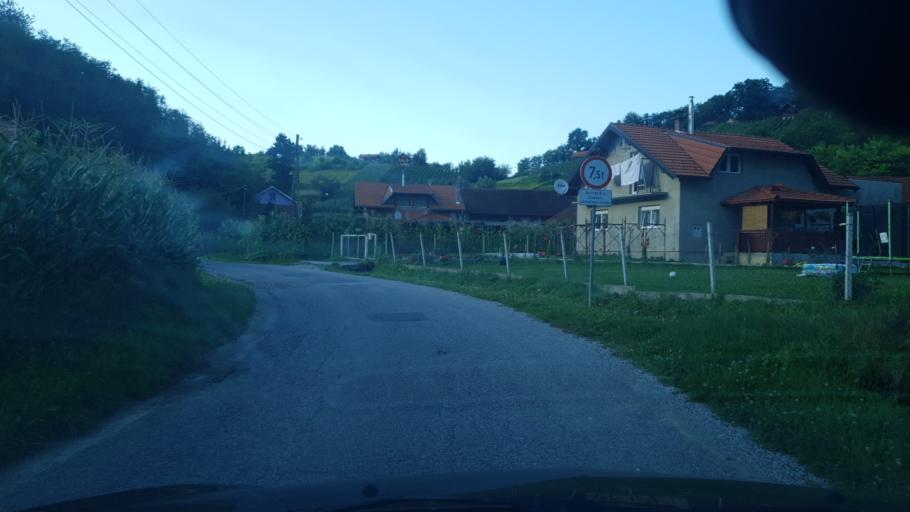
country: HR
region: Krapinsko-Zagorska
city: Zabok
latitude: 46.0587
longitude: 15.8903
